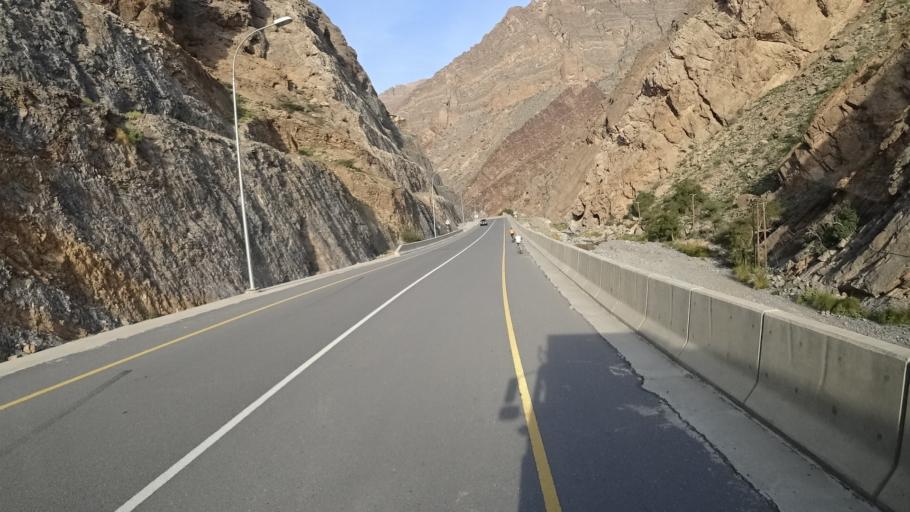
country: OM
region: Al Batinah
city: Bayt al `Awabi
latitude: 23.2776
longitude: 57.4604
